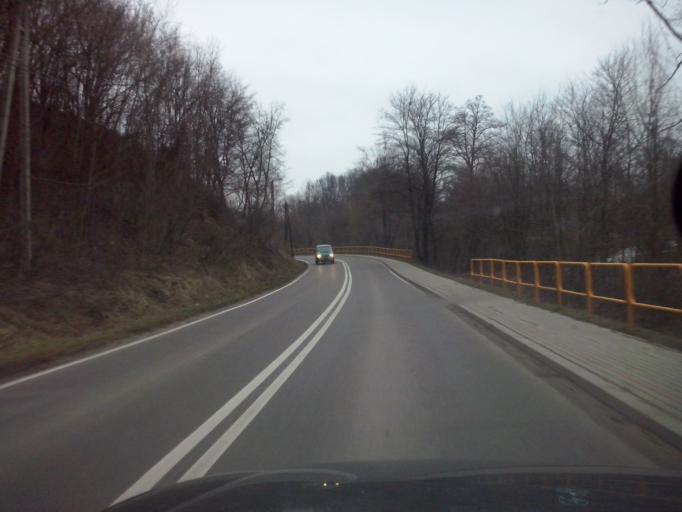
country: PL
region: Subcarpathian Voivodeship
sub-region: Powiat nizanski
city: Krzeszow
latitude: 50.4073
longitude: 22.3425
